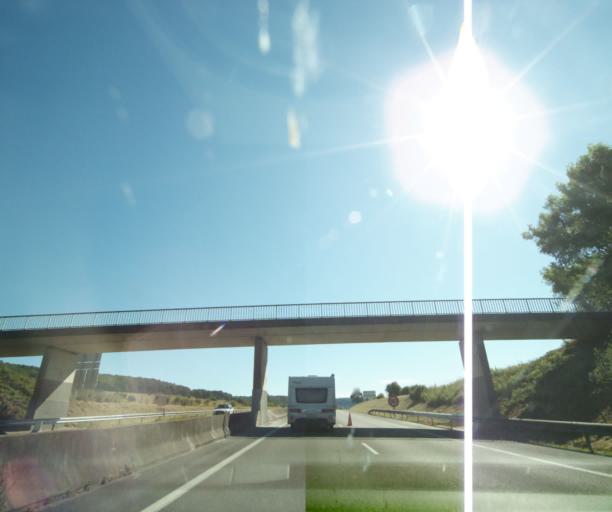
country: FR
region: Champagne-Ardenne
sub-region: Departement de la Haute-Marne
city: Rolampont
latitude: 47.9469
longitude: 5.3105
